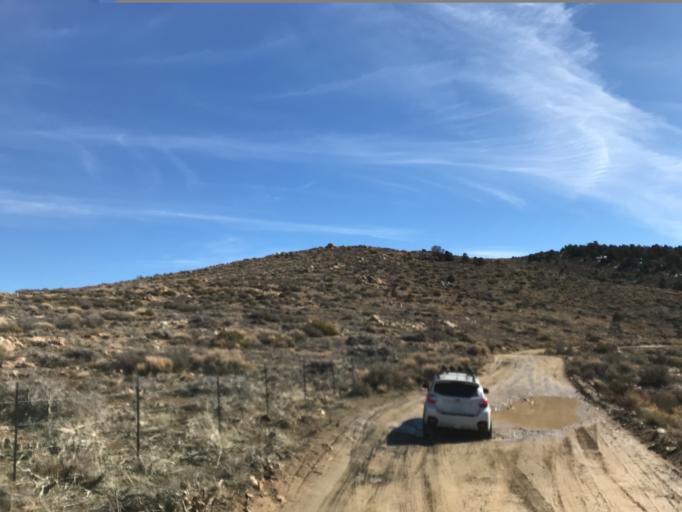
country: US
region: California
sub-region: San Bernardino County
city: Big Bear City
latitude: 34.2792
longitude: -116.7858
